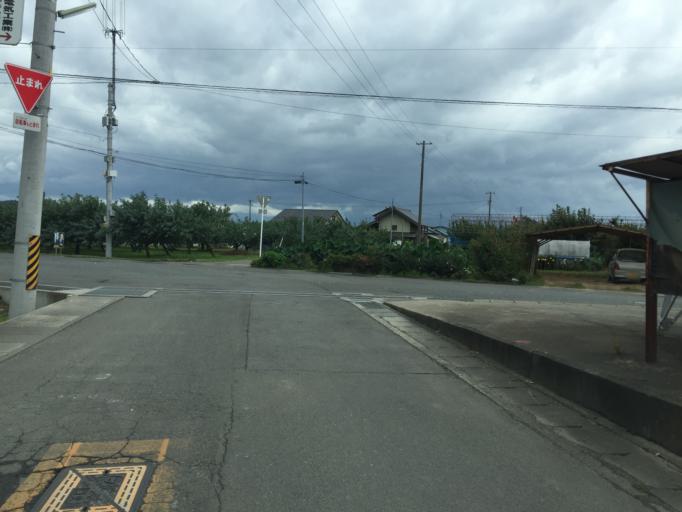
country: JP
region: Fukushima
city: Hobaramachi
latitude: 37.8287
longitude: 140.5444
